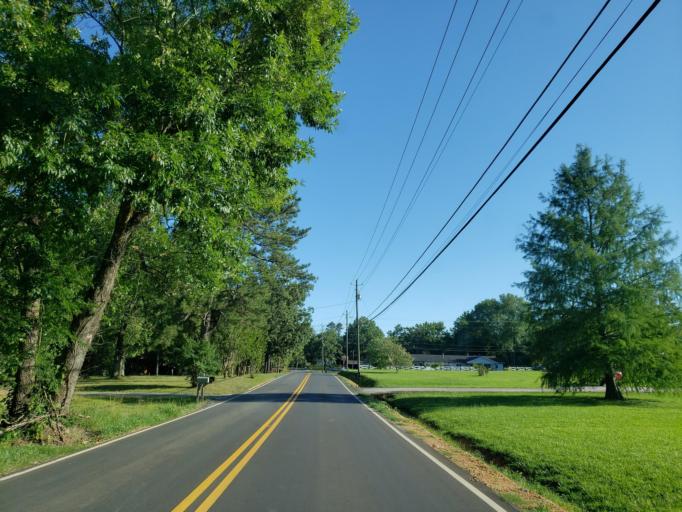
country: US
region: Georgia
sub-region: Floyd County
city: Rome
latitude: 34.3217
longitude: -85.1639
